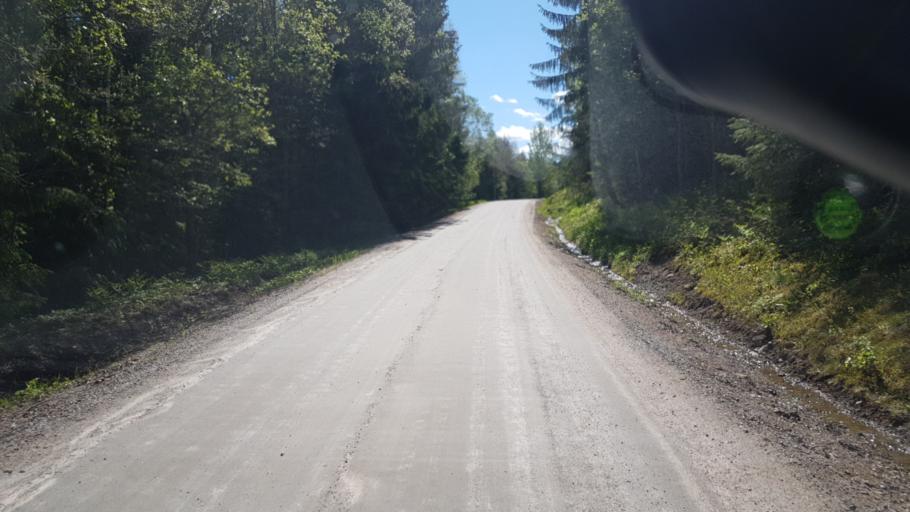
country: SE
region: Vaermland
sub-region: Arvika Kommun
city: Arvika
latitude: 59.6627
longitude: 12.7602
